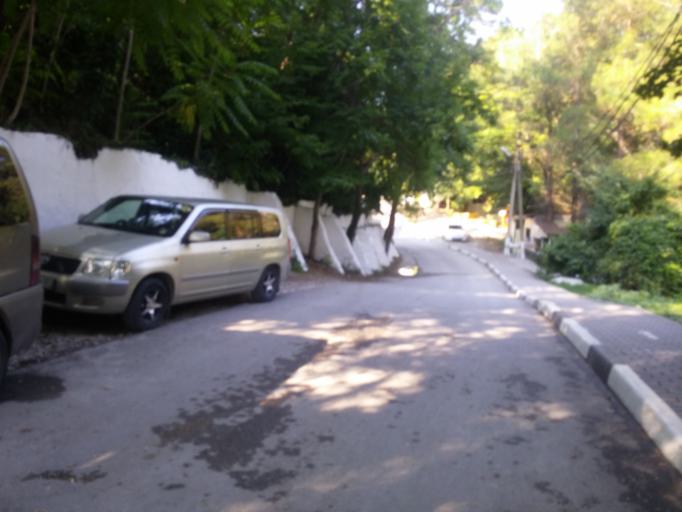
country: RU
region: Krasnodarskiy
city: Divnomorskoye
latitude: 44.4643
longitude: 38.1551
